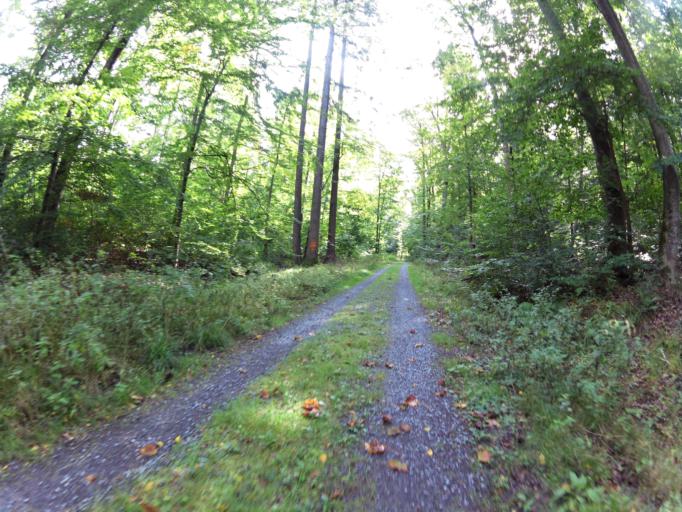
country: DE
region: Bavaria
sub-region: Regierungsbezirk Unterfranken
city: Waldbrunn
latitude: 49.7243
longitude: 9.8062
